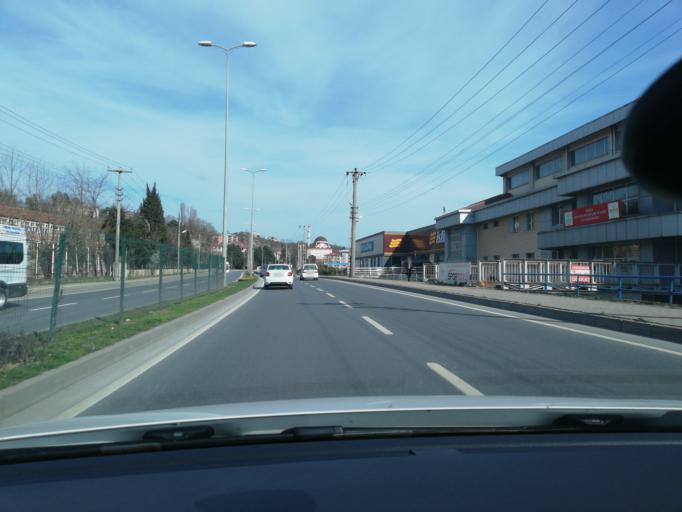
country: TR
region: Zonguldak
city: Eregli
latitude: 41.2691
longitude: 31.4419
